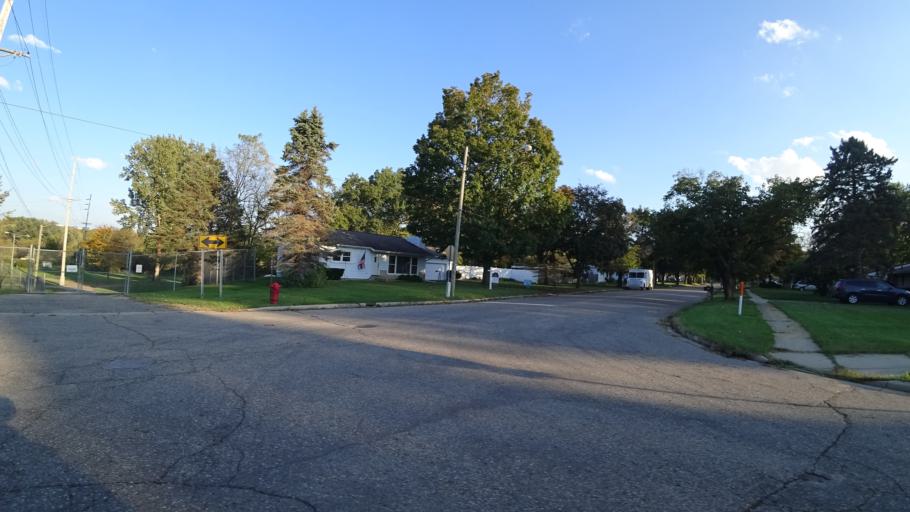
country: US
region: Michigan
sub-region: Saint Joseph County
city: Three Rivers
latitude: 41.9493
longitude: -85.6433
